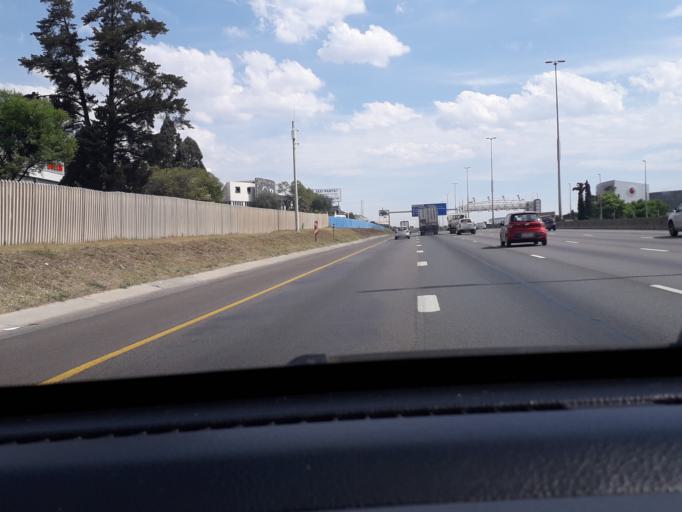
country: ZA
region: Gauteng
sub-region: City of Johannesburg Metropolitan Municipality
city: Midrand
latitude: -25.9683
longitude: 28.1302
